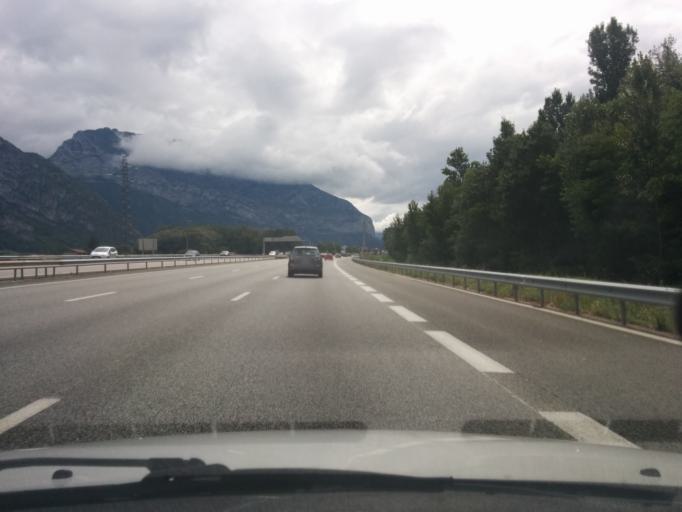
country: FR
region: Rhone-Alpes
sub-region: Departement de l'Isere
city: Noyarey
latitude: 45.2555
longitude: 5.6446
